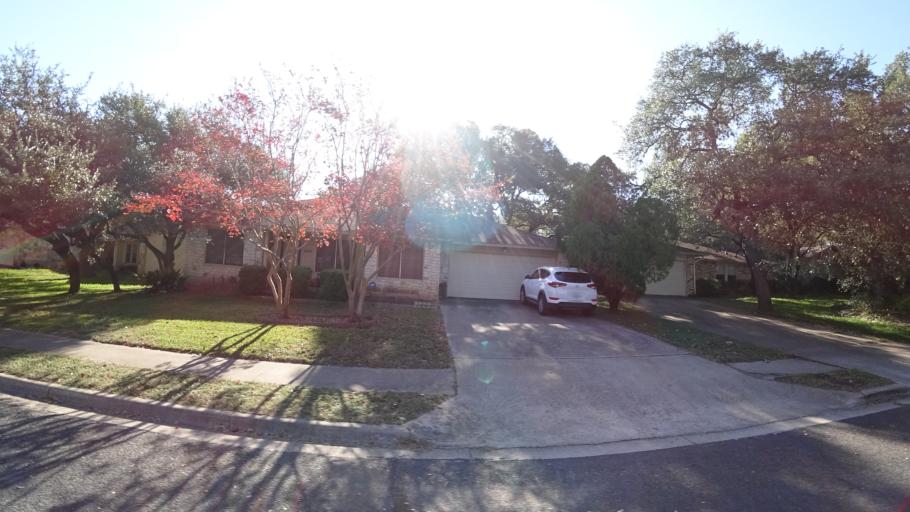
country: US
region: Texas
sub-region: Travis County
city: Barton Creek
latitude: 30.2274
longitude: -97.8400
